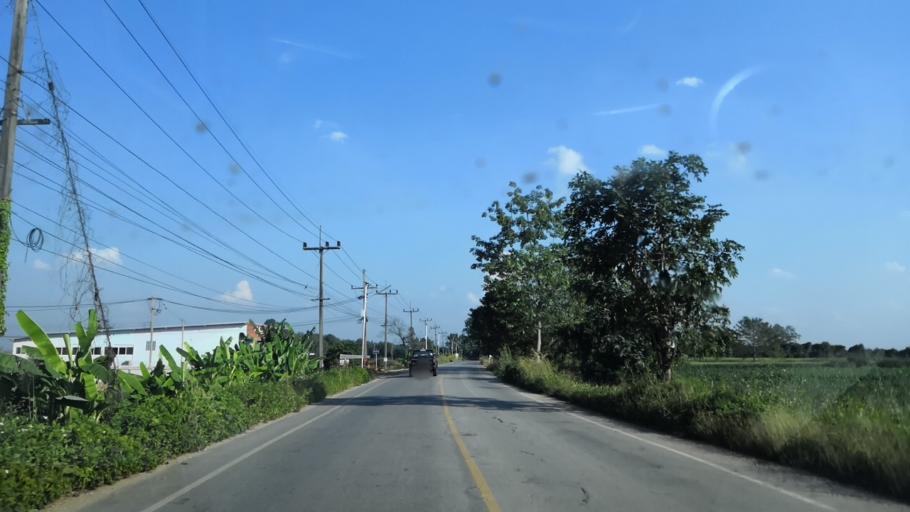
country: TH
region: Chiang Rai
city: Chiang Rai
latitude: 19.9339
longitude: 99.8828
